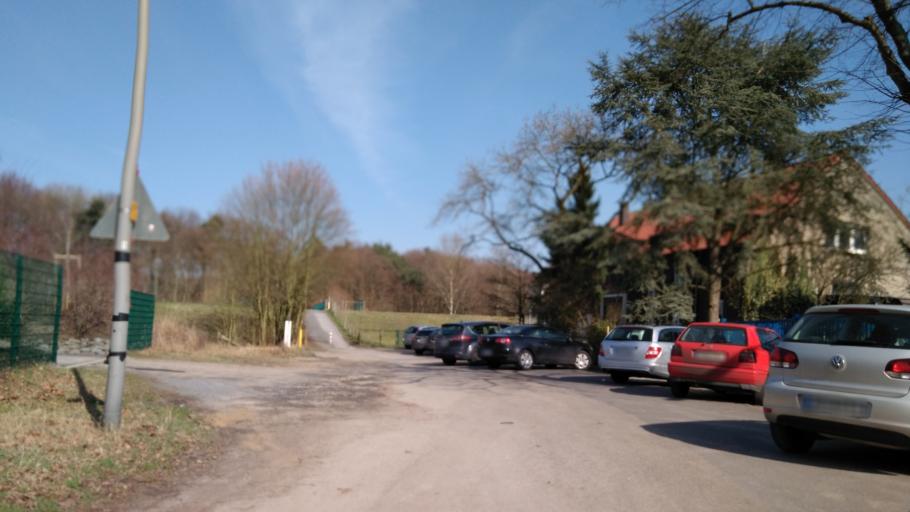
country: DE
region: North Rhine-Westphalia
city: Dorsten
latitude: 51.6575
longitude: 6.9870
